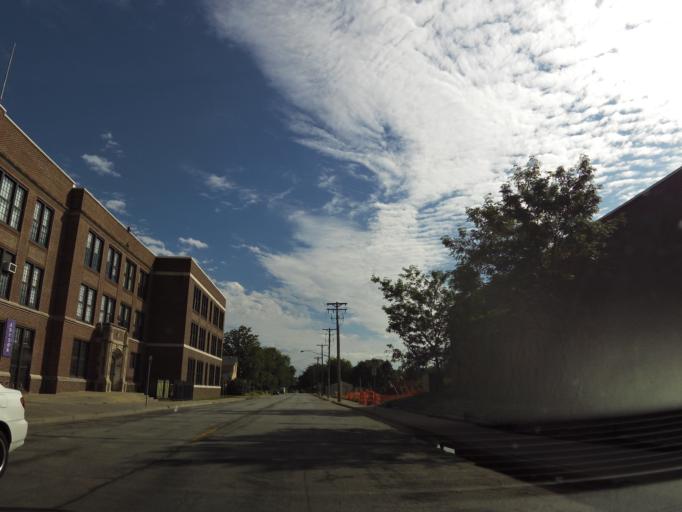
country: US
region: Minnesota
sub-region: Hennepin County
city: Minneapolis
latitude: 45.0098
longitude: -93.2526
